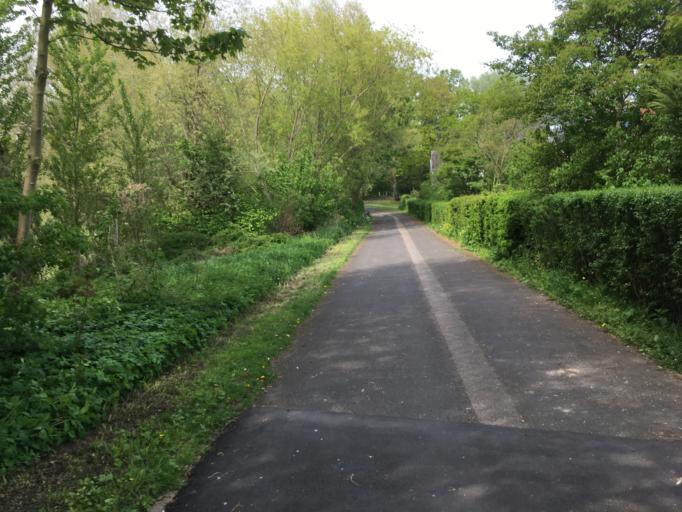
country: DE
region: Lower Saxony
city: Braunschweig
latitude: 52.2923
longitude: 10.5039
